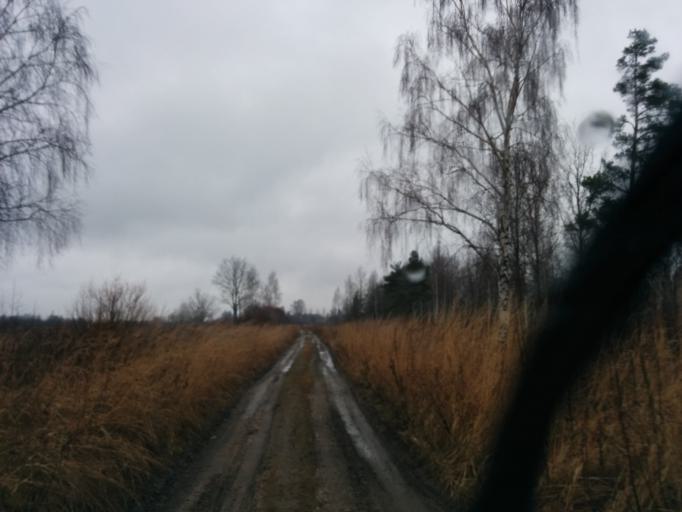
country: LV
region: Jelgava
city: Jelgava
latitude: 56.6768
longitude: 23.7102
